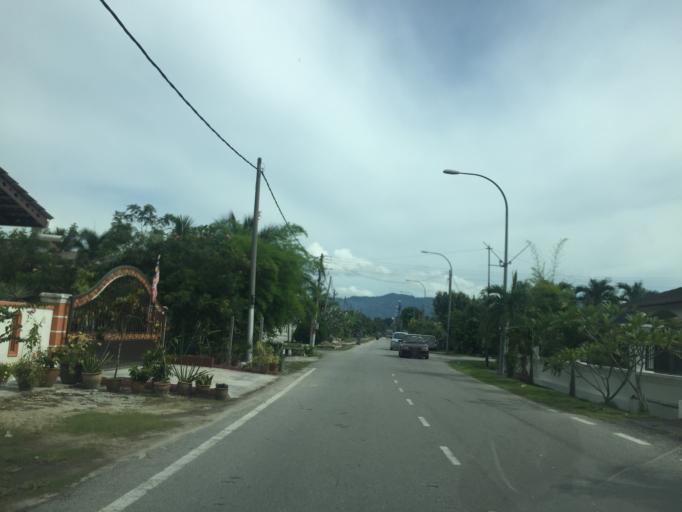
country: MY
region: Negeri Sembilan
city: Seremban
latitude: 2.7293
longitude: 101.9658
